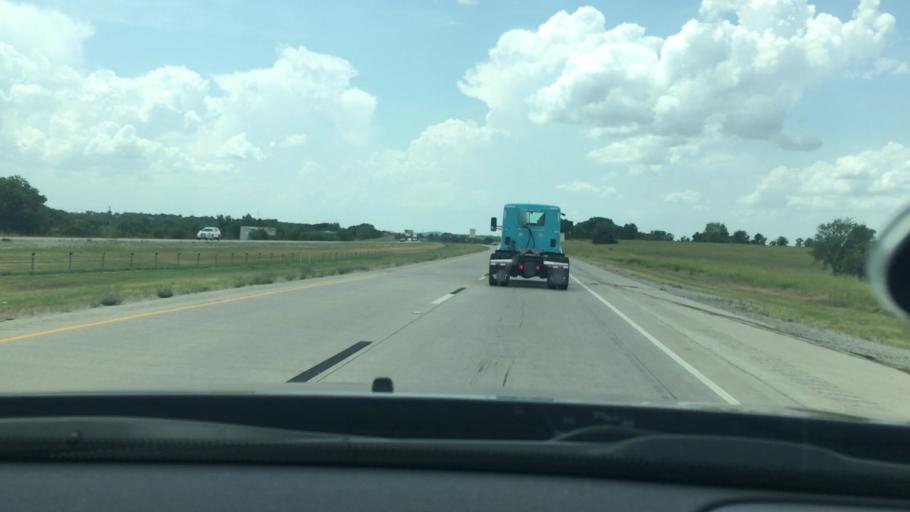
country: US
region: Oklahoma
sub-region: Carter County
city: Ardmore
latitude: 34.1306
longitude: -97.1566
